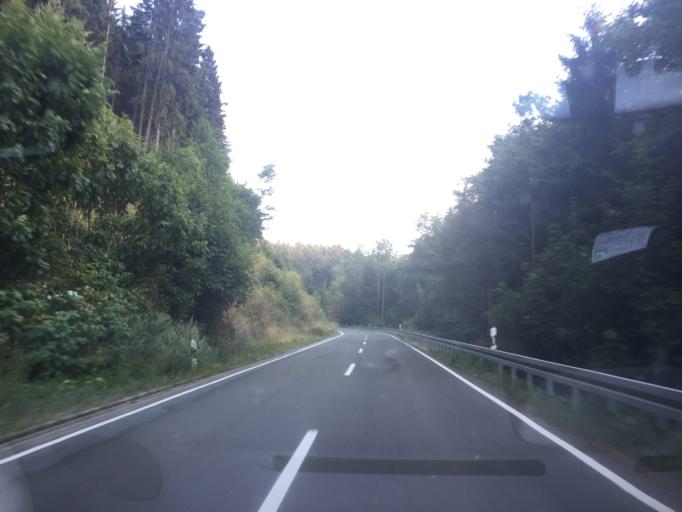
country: DE
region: Saxony-Anhalt
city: Darlingerode
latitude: 51.7943
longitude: 10.7360
